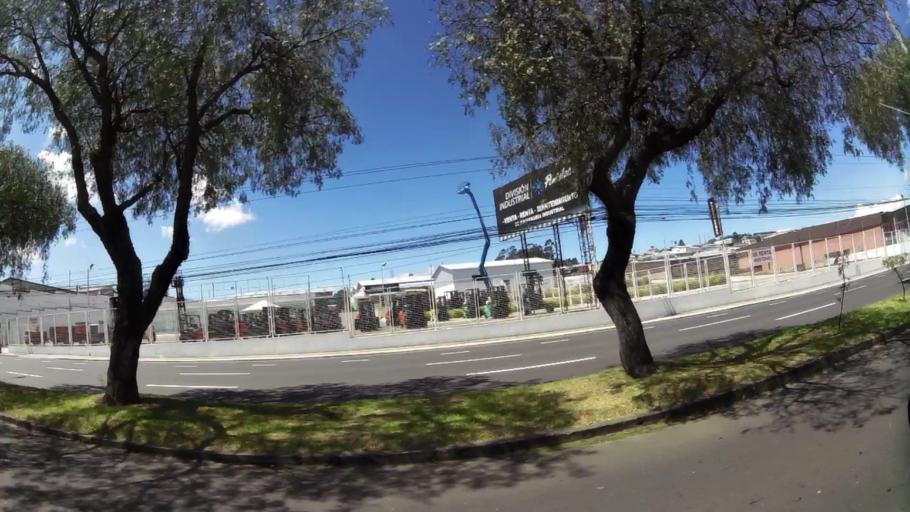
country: EC
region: Pichincha
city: Quito
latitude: -0.1083
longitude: -78.4777
